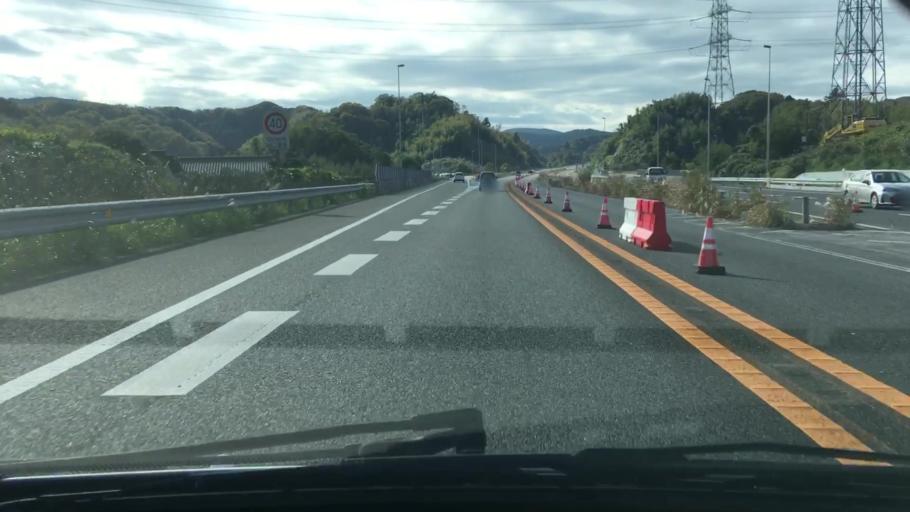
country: JP
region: Chiba
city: Kimitsu
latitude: 35.2859
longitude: 139.9278
